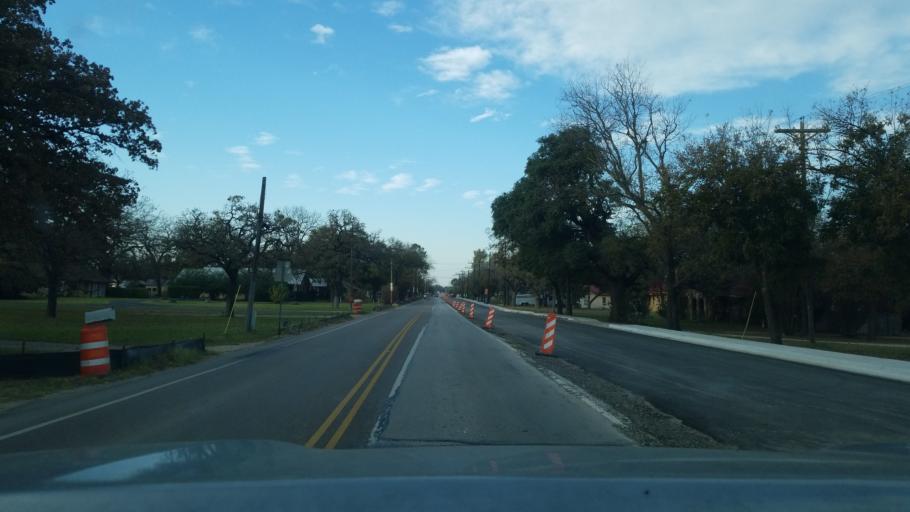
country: US
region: Texas
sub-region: Brown County
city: Lake Brownwood
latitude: 32.0870
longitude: -98.9641
